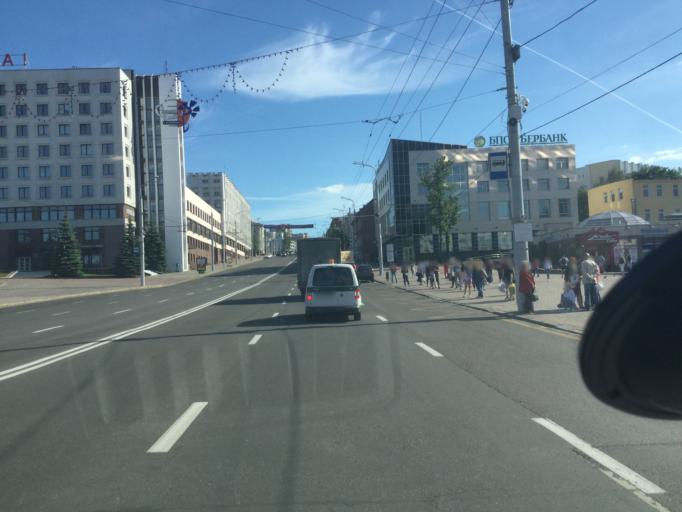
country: BY
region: Vitebsk
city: Vitebsk
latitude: 55.1917
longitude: 30.2060
